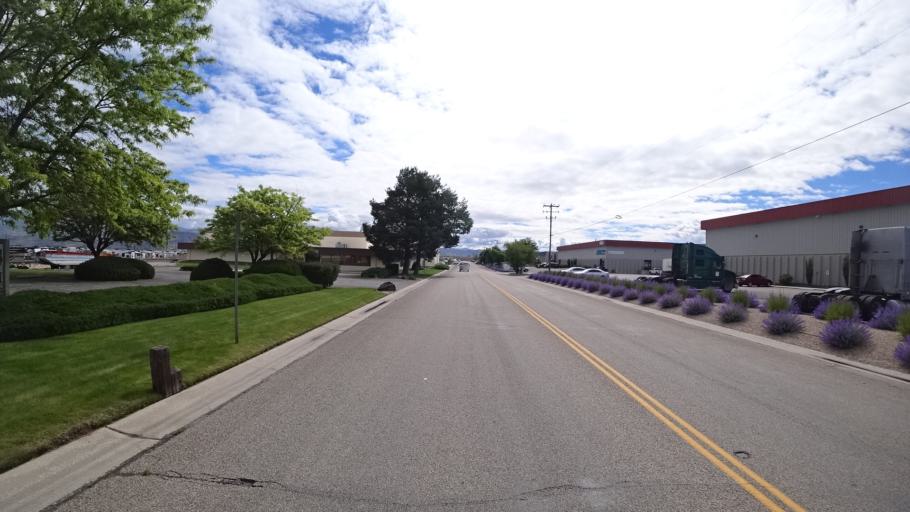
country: US
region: Idaho
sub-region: Ada County
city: Boise
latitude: 43.5629
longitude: -116.1956
